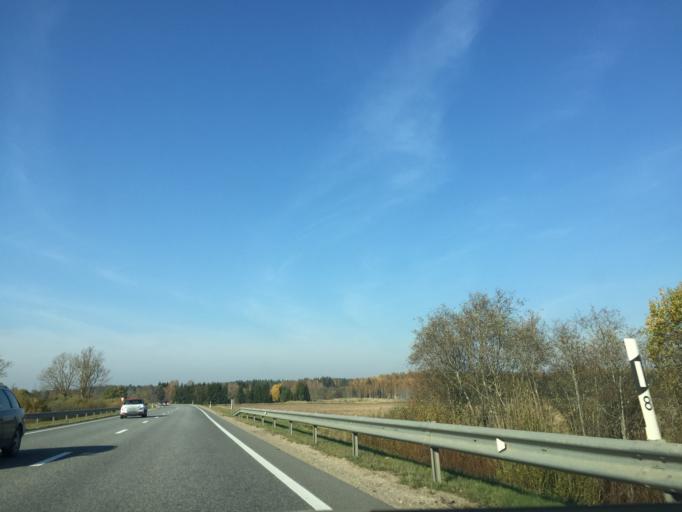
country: LV
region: Broceni
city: Broceni
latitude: 56.6711
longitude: 22.5886
